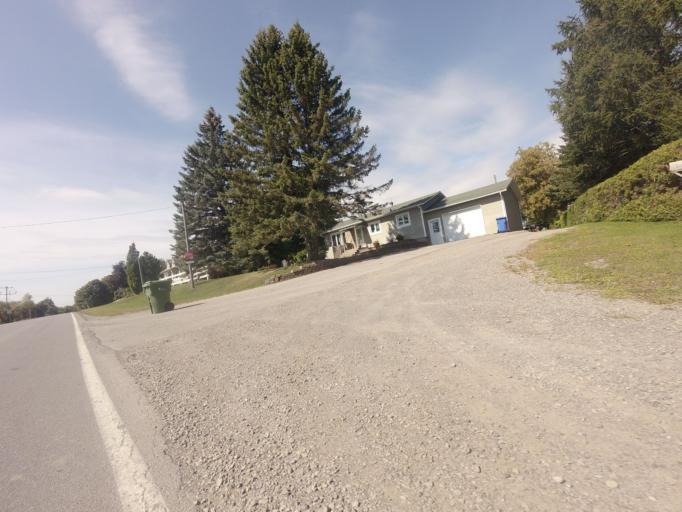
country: CA
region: Quebec
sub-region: Laurentides
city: Saint-Eustache
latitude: 45.5951
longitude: -73.9141
